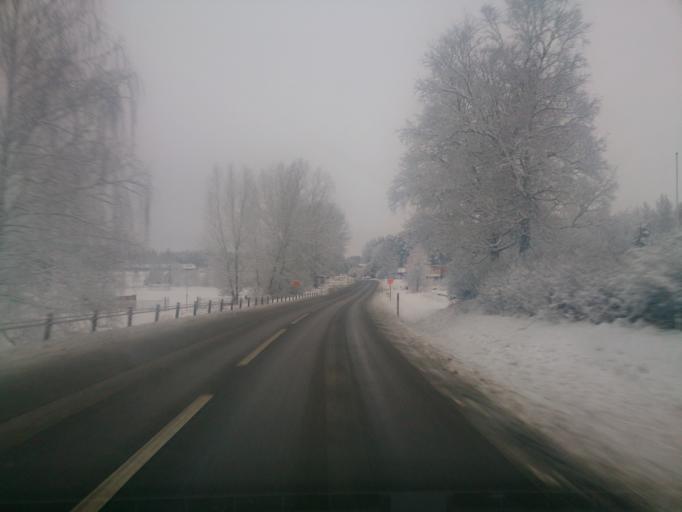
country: SE
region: OEstergoetland
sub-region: Linkopings Kommun
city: Sturefors
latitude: 58.3100
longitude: 15.8784
